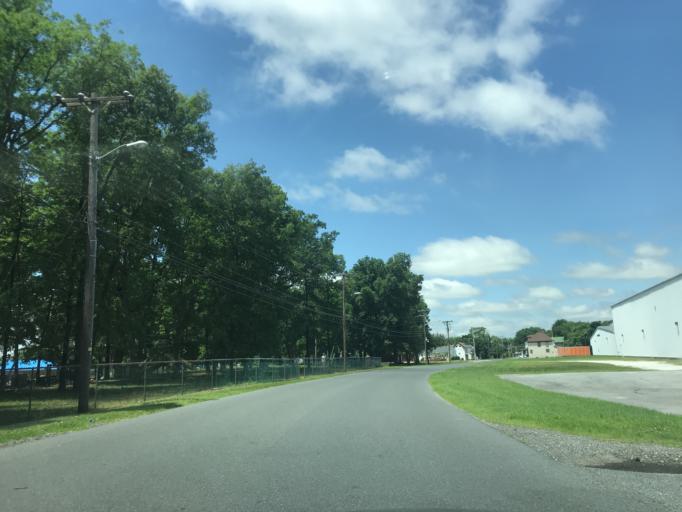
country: US
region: Maryland
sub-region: Caroline County
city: Federalsburg
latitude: 38.6930
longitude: -75.7635
